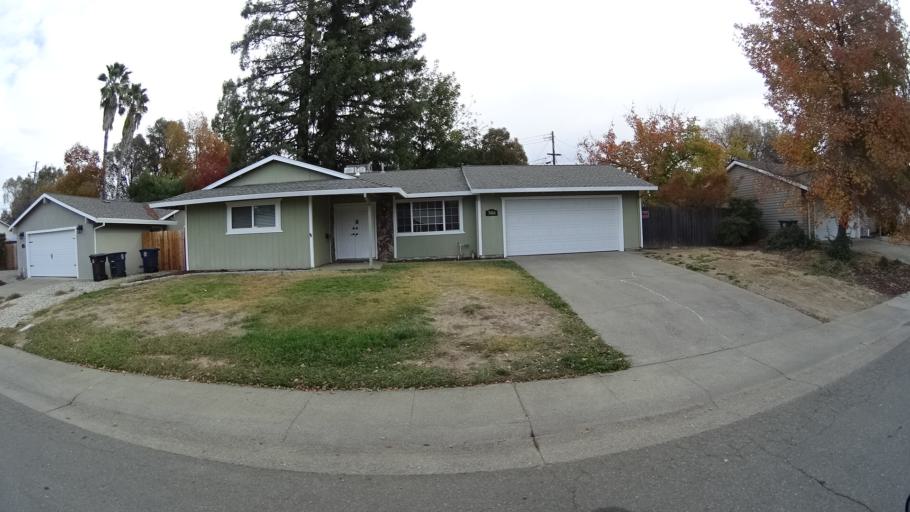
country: US
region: California
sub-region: Sacramento County
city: Citrus Heights
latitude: 38.7000
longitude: -121.2749
